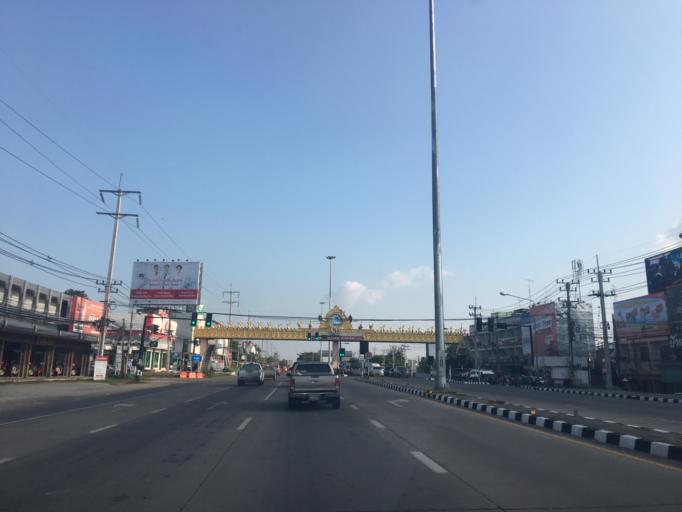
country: TH
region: Phayao
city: Phayao
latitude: 19.1718
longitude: 99.9062
